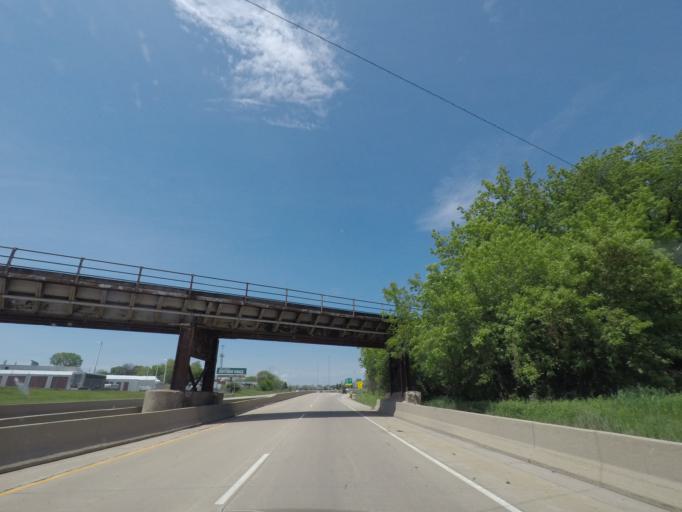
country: US
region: Wisconsin
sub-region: Dane County
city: Madison
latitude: 43.0335
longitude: -89.3909
